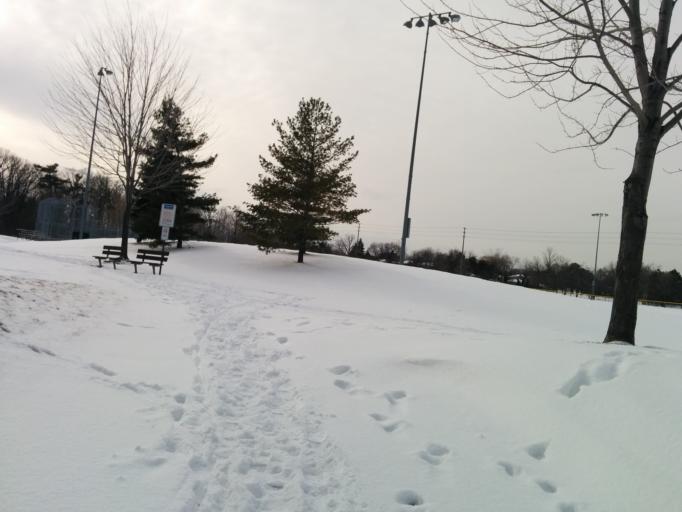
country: CA
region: Ontario
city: Mississauga
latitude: 43.5251
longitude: -79.6598
